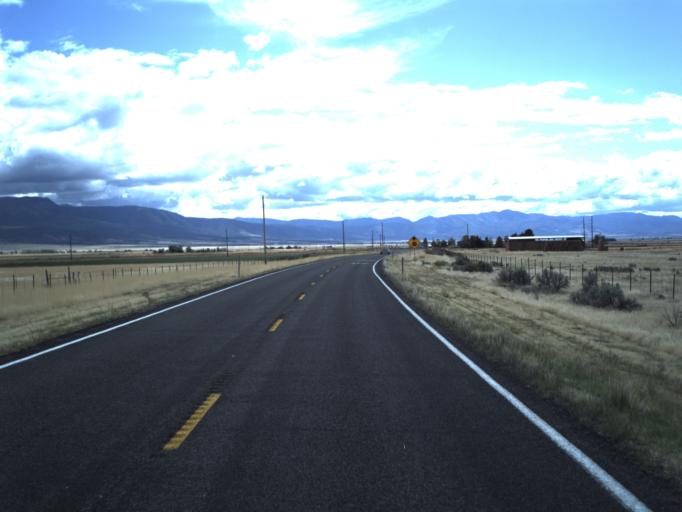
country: US
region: Utah
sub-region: Millard County
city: Fillmore
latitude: 38.9843
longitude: -112.4100
